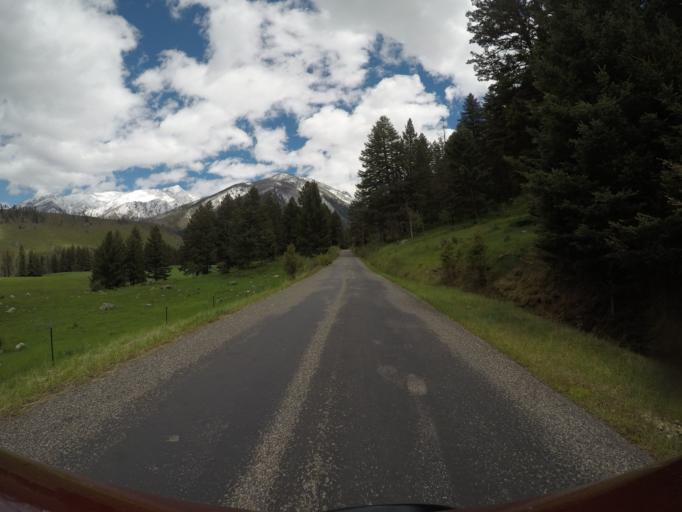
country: US
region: Montana
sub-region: Park County
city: Livingston
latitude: 45.4997
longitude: -110.5403
